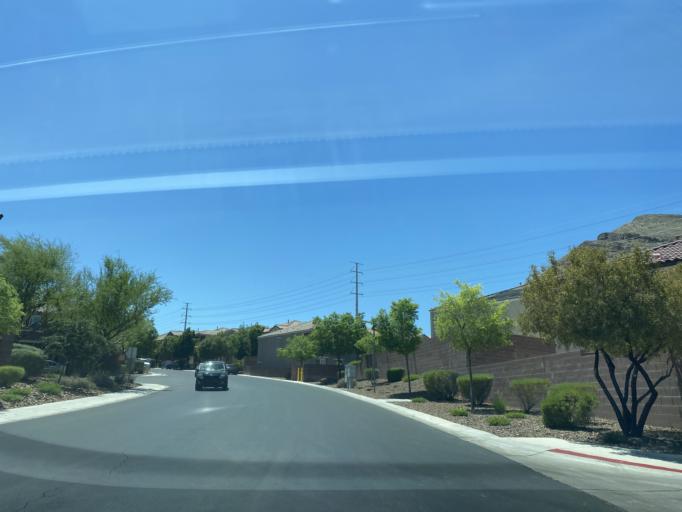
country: US
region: Nevada
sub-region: Clark County
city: Summerlin South
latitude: 36.2271
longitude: -115.3285
